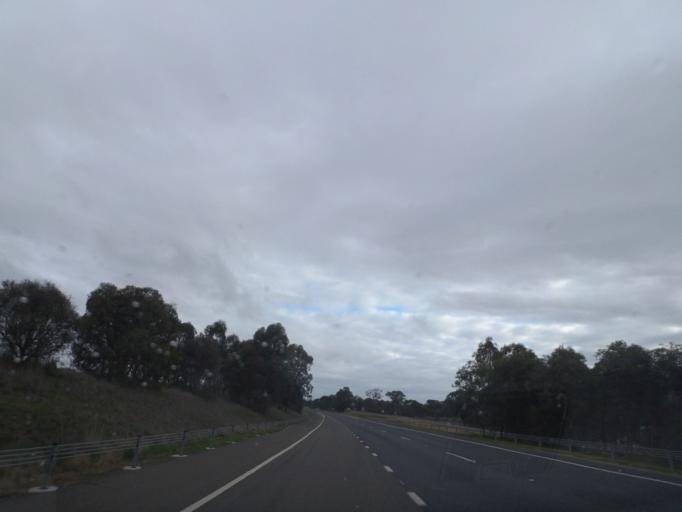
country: AU
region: Victoria
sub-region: Wangaratta
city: Wangaratta
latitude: -36.2247
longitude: 146.4439
